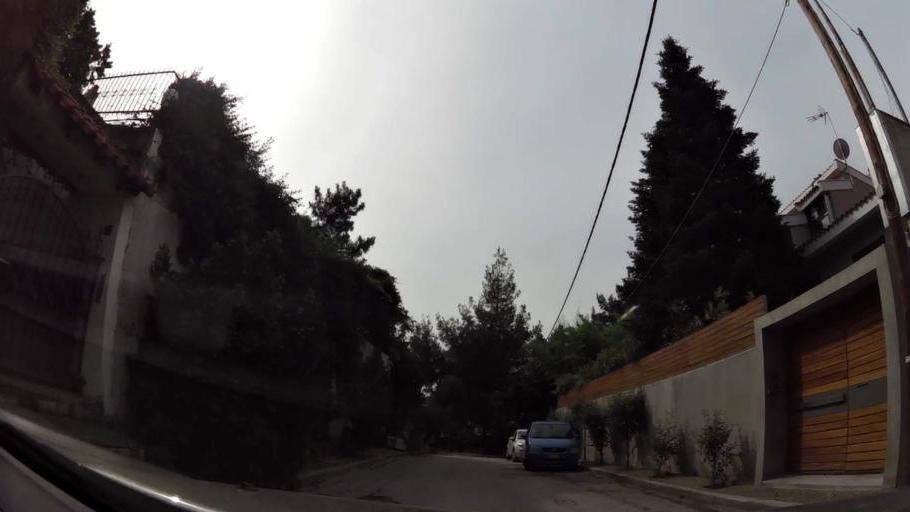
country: GR
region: Central Macedonia
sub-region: Nomos Thessalonikis
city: Panorama
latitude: 40.5836
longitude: 23.0314
